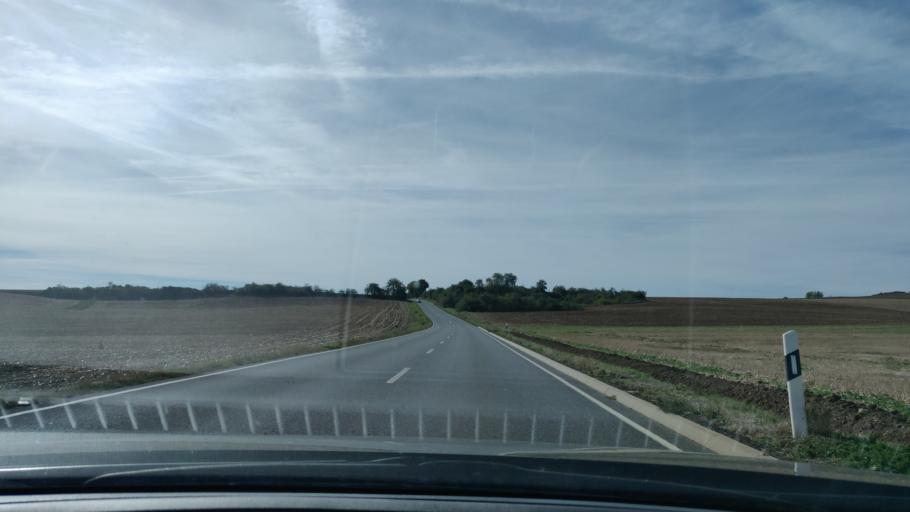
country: DE
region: Hesse
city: Fritzlar
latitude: 51.1520
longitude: 9.2741
